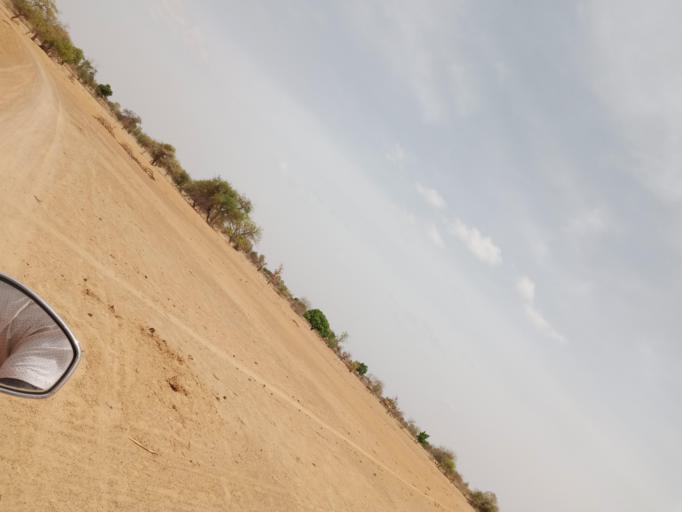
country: BF
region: Est
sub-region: Gnagna Province
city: Bogande
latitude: 13.0980
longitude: -0.0484
